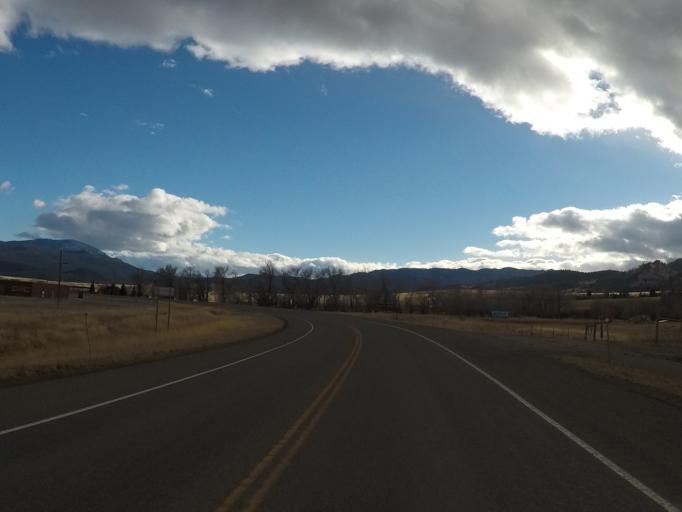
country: US
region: Montana
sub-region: Jefferson County
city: Boulder
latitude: 46.2291
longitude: -112.1222
